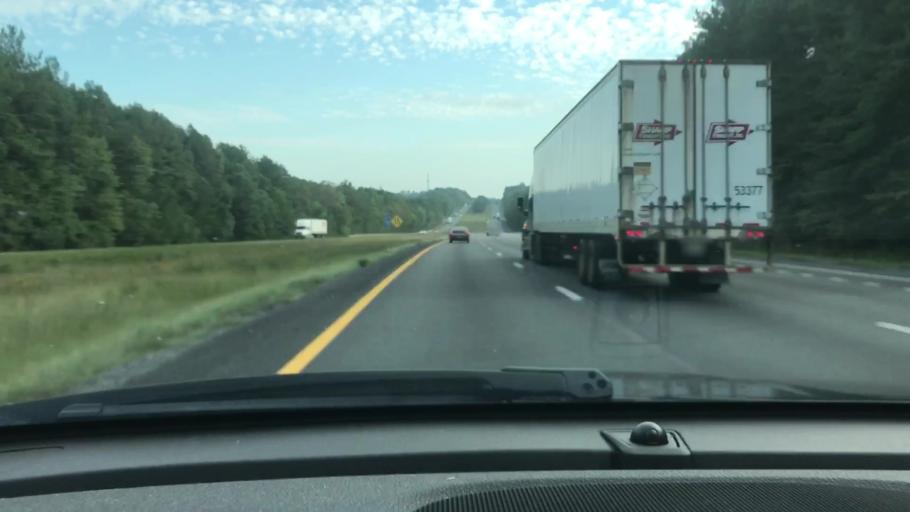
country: US
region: Tennessee
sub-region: Sumner County
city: Millersville
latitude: 36.4238
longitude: -86.7144
